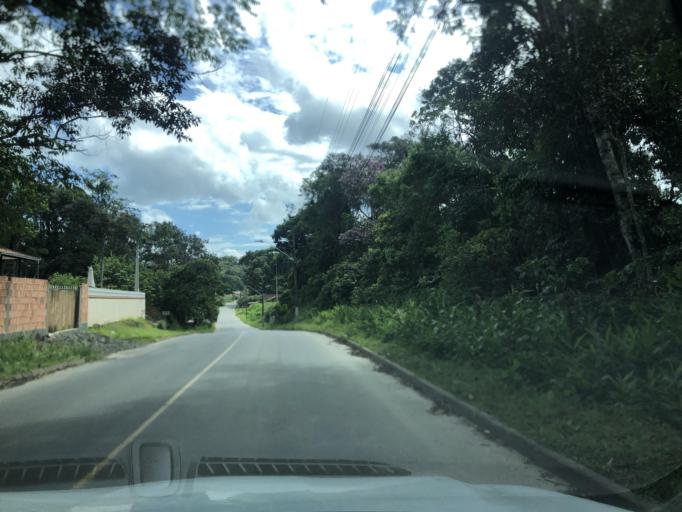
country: BR
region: Santa Catarina
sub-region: Sao Francisco Do Sul
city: Sao Francisco do Sul
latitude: -26.2279
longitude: -48.6042
